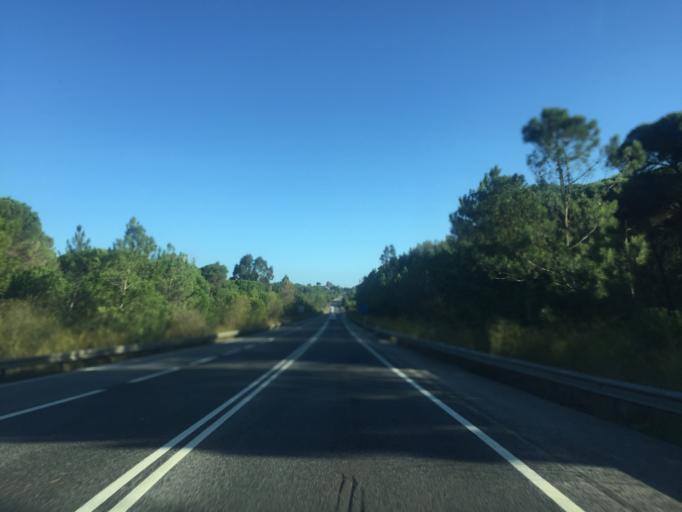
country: PT
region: Lisbon
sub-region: Azambuja
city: Alcoentre
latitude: 39.2624
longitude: -8.9493
